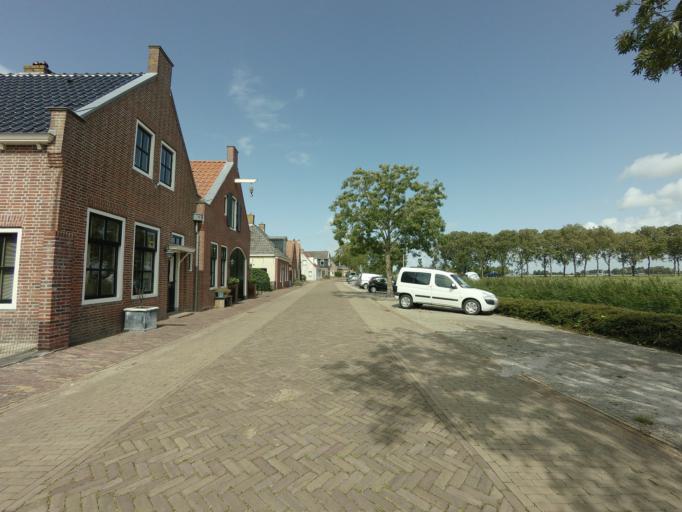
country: NL
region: Friesland
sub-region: Gemeente Harlingen
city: Harlingen
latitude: 53.1143
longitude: 5.4415
